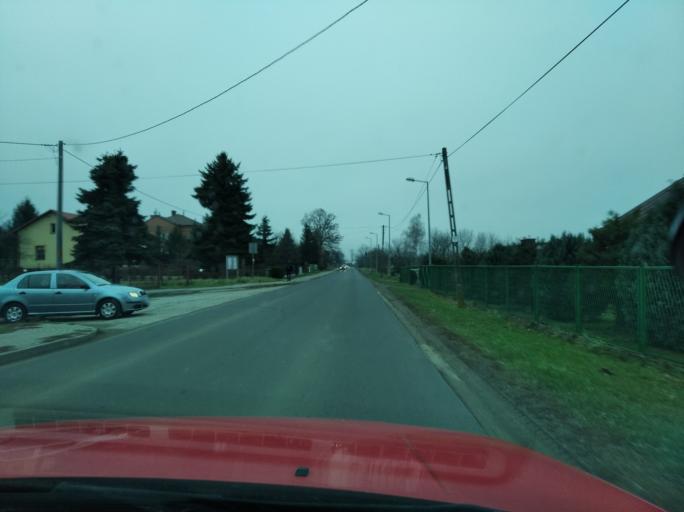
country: PL
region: Subcarpathian Voivodeship
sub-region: Powiat jaroslawski
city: Pawlosiow
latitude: 50.0119
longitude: 22.6495
